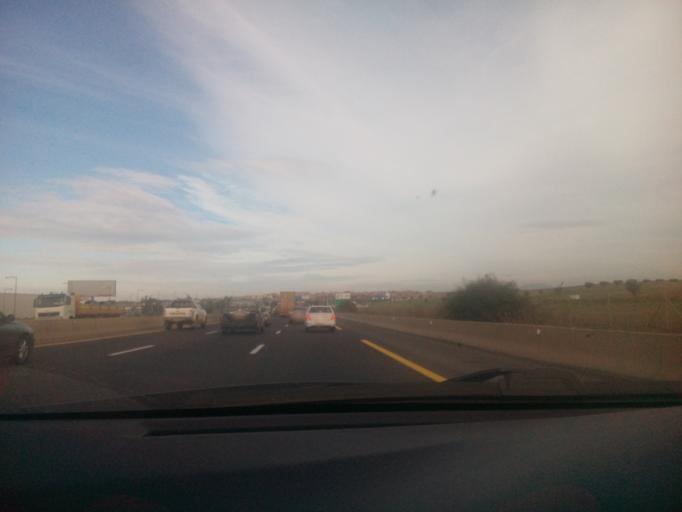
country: DZ
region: Oran
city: Es Senia
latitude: 35.5913
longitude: -0.5719
